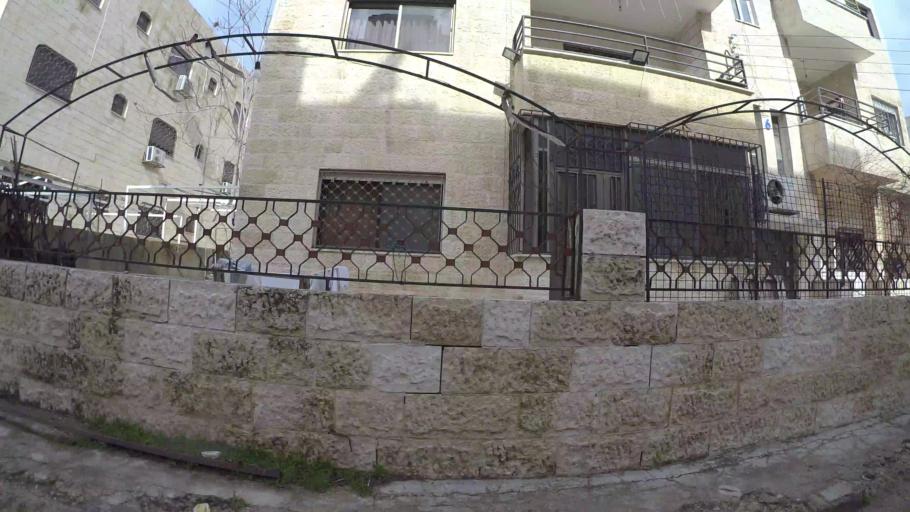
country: JO
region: Amman
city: Wadi as Sir
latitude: 31.9482
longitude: 35.8405
